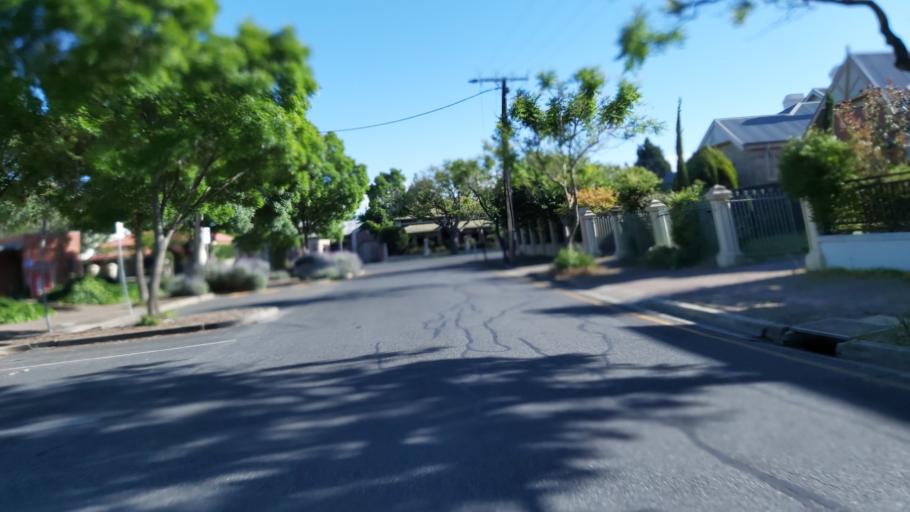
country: AU
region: South Australia
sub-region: Unley
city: Unley
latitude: -34.9496
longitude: 138.6128
